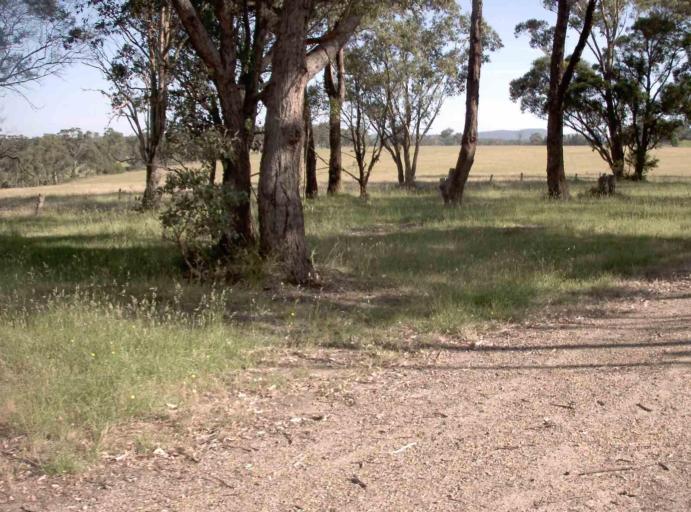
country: AU
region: Victoria
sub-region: East Gippsland
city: Lakes Entrance
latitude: -37.6966
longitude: 148.4652
